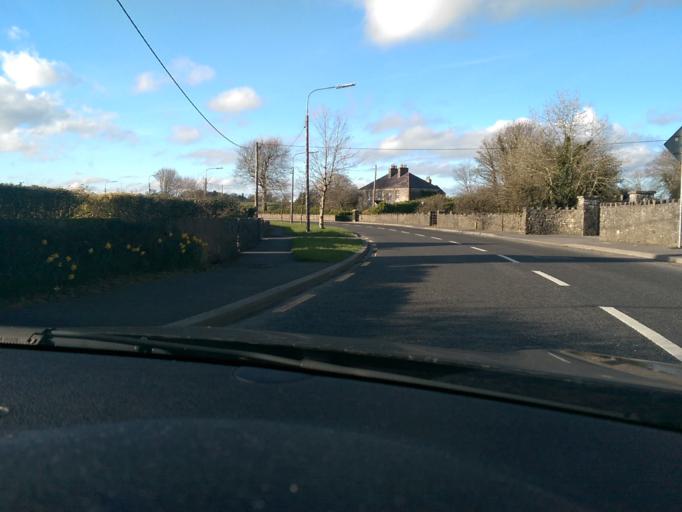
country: IE
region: Connaught
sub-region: Roscommon
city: Roscommon
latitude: 53.6389
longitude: -8.1911
